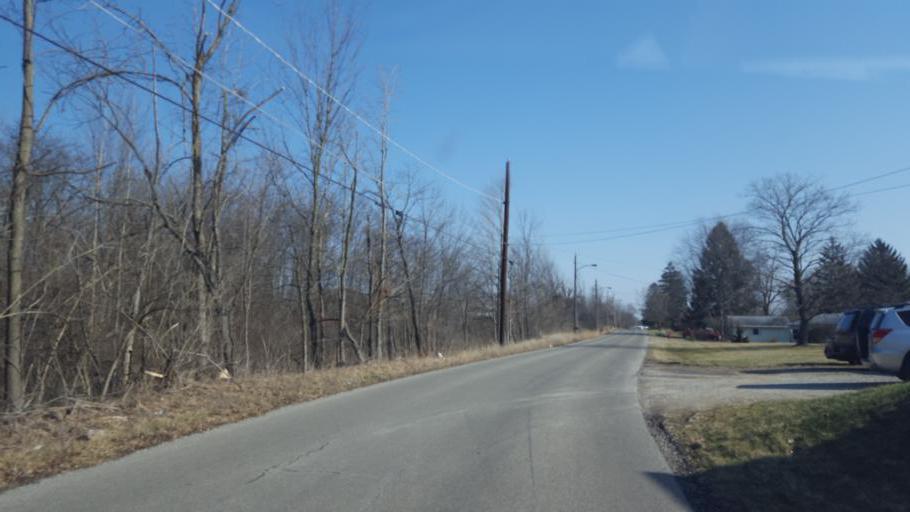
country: US
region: Ohio
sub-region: Crawford County
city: Galion
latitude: 40.7353
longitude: -82.7690
